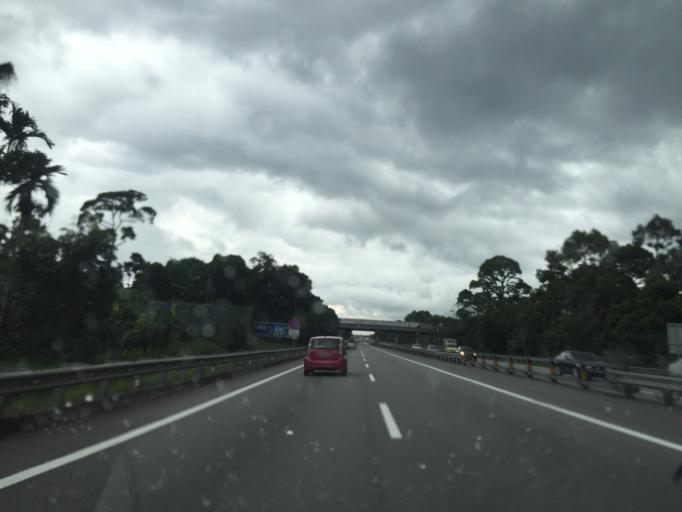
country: MY
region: Perak
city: Taiping
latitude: 4.7735
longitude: 100.7690
